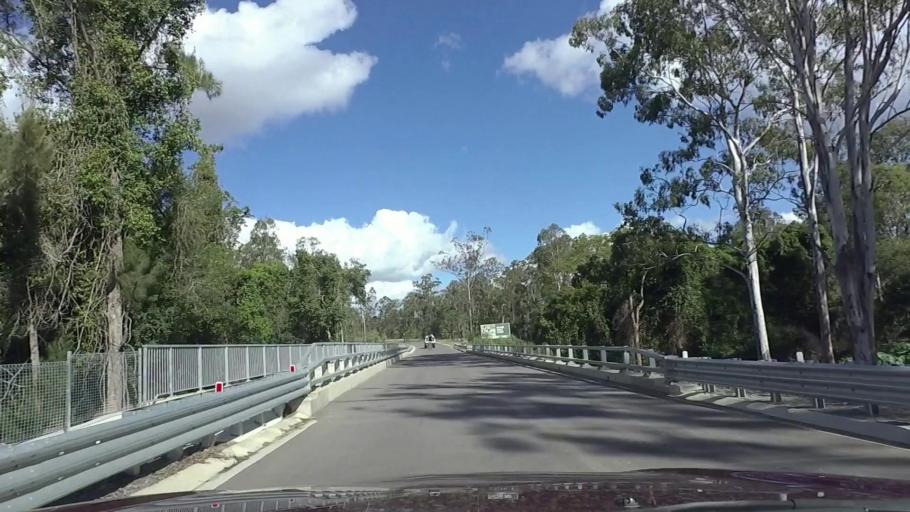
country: AU
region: Queensland
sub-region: Ipswich
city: Springfield Lakes
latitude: -27.7461
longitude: 152.9205
